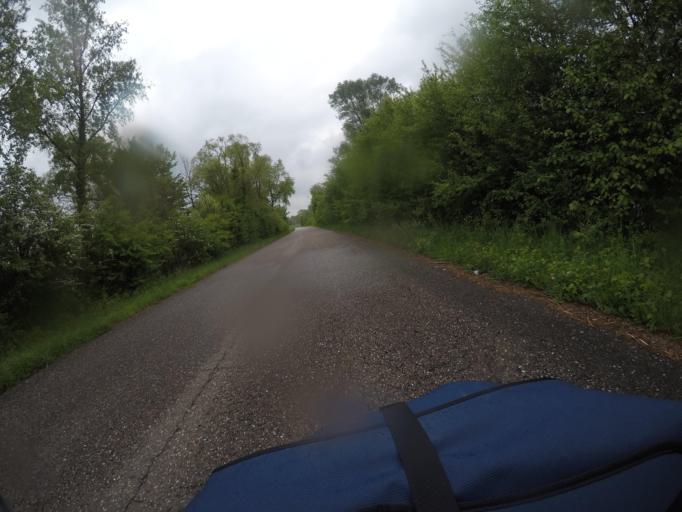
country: DE
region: Baden-Wuerttemberg
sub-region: Karlsruhe Region
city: Hugelsheim
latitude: 48.8267
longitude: 8.1014
